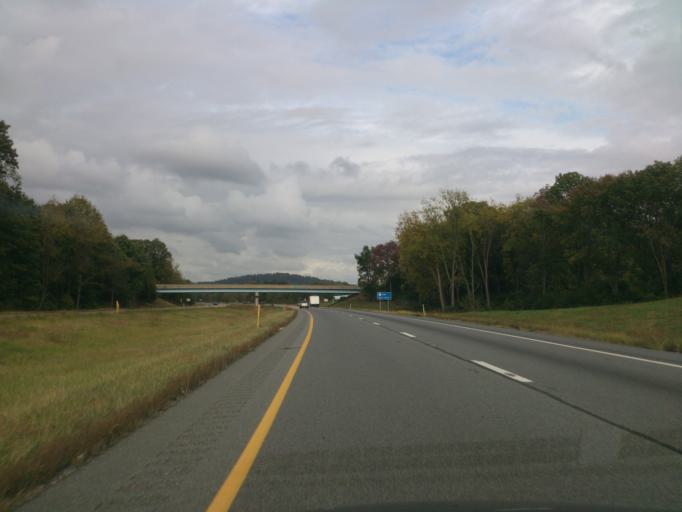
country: US
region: Pennsylvania
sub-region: Lancaster County
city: Adamstown
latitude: 40.2266
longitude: -76.0569
